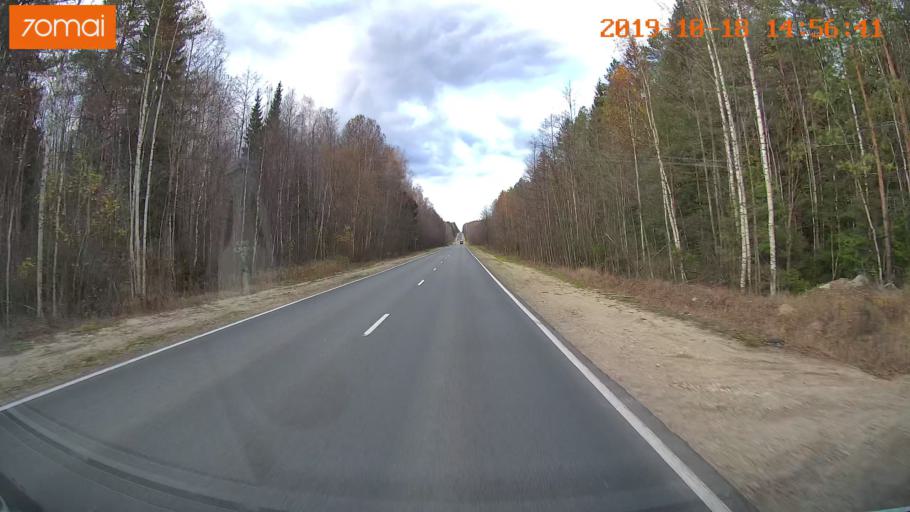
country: RU
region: Vladimir
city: Kurlovo
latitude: 55.4682
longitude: 40.5860
